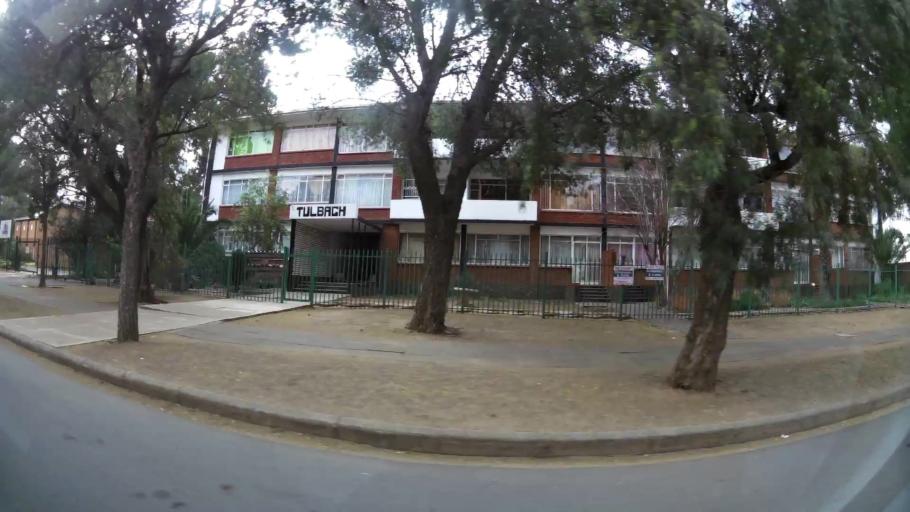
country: ZA
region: Orange Free State
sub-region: Mangaung Metropolitan Municipality
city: Bloemfontein
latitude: -29.1097
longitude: 26.2236
